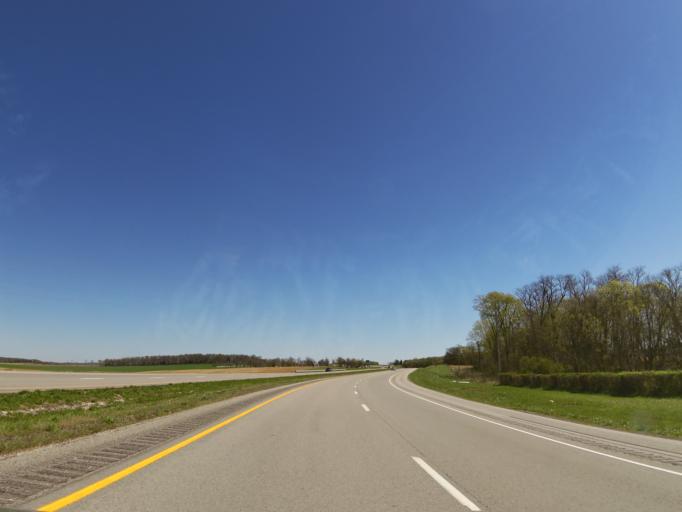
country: US
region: Kentucky
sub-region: Logan County
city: Auburn
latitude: 36.8744
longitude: -86.6823
